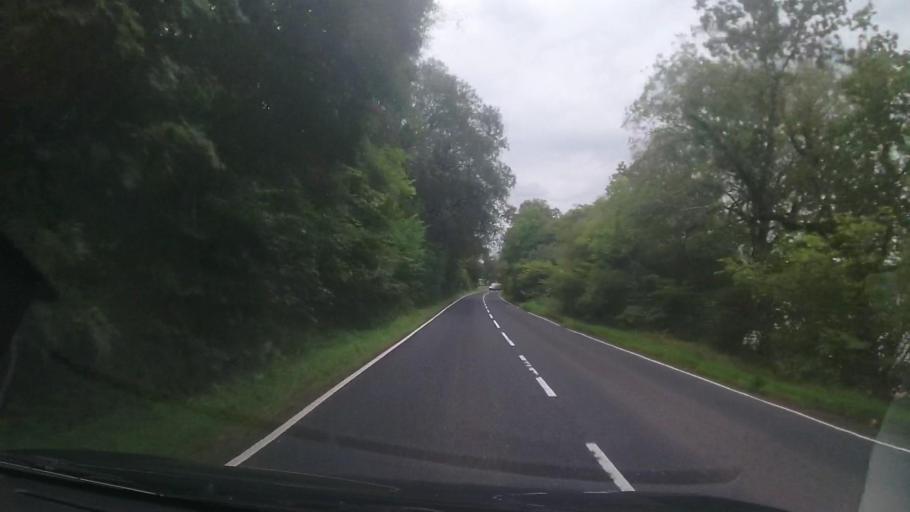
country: GB
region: Scotland
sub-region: Argyll and Bute
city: Garelochhead
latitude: 56.2255
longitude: -5.0240
